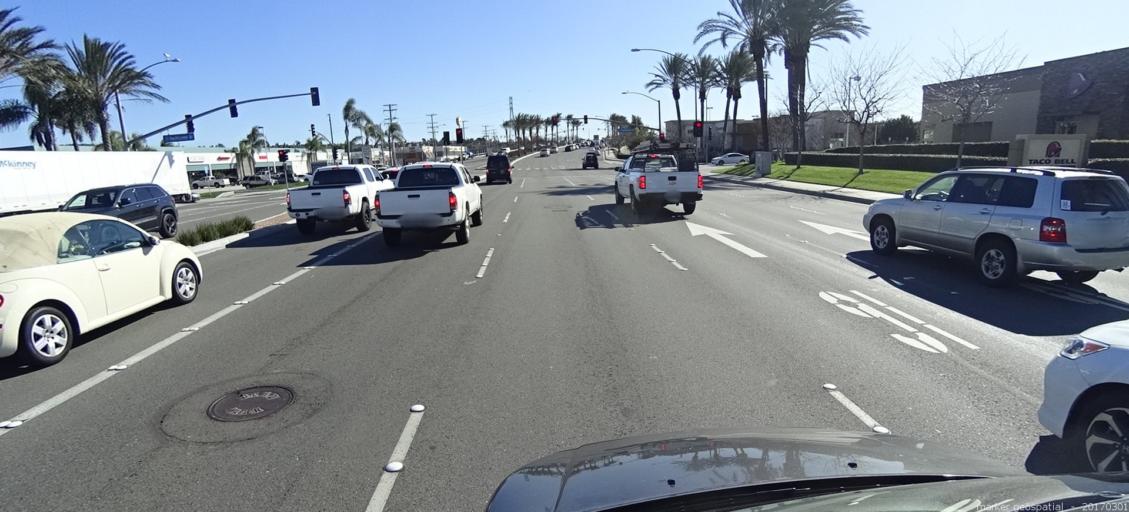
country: US
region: California
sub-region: Orange County
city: Placentia
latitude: 33.8545
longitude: -117.8375
